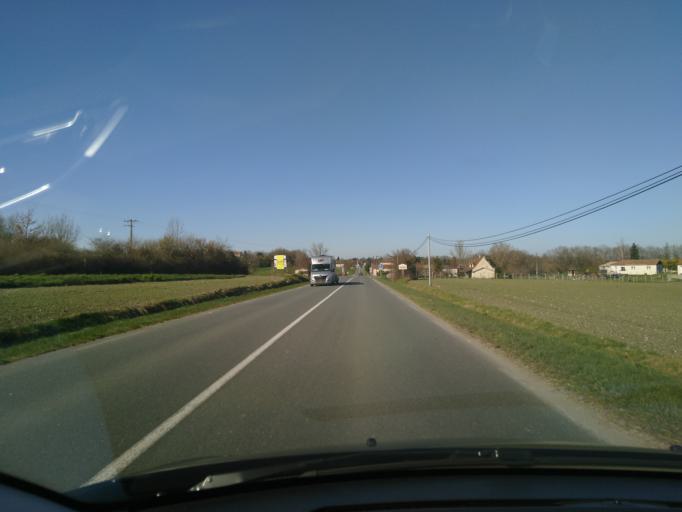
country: FR
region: Aquitaine
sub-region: Departement de la Dordogne
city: Monbazillac
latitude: 44.7498
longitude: 0.5353
